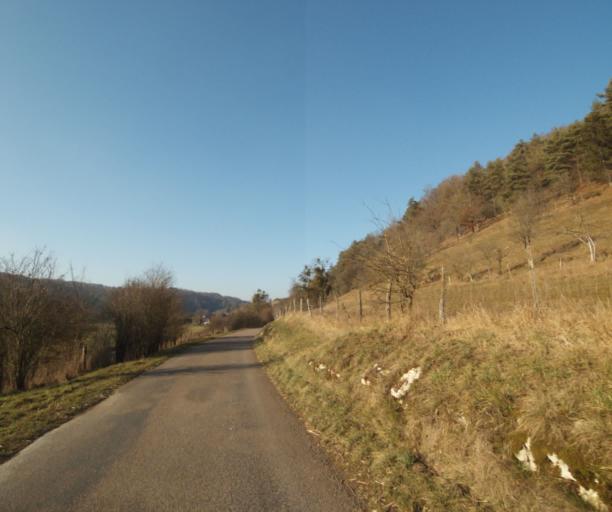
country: FR
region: Champagne-Ardenne
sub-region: Departement de la Haute-Marne
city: Joinville
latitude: 48.4898
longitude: 5.2005
